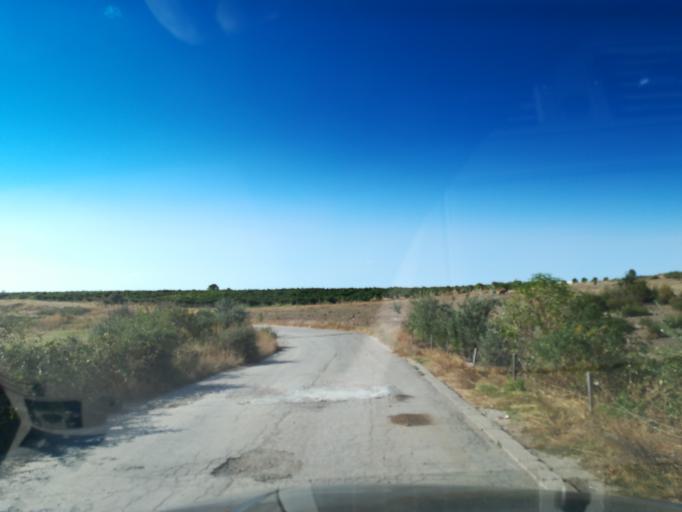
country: BG
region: Khaskovo
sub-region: Obshtina Mineralni Bani
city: Mineralni Bani
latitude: 41.9718
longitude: 25.3496
